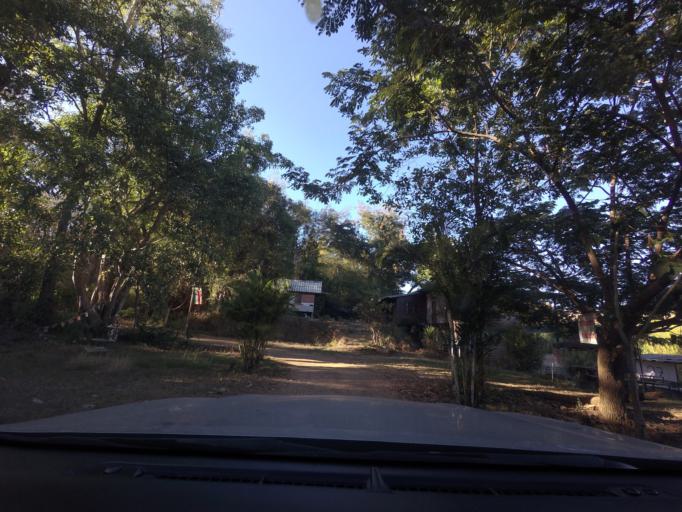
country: TH
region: Mae Hong Son
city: Wiang Nuea
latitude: 19.4033
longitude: 98.4174
